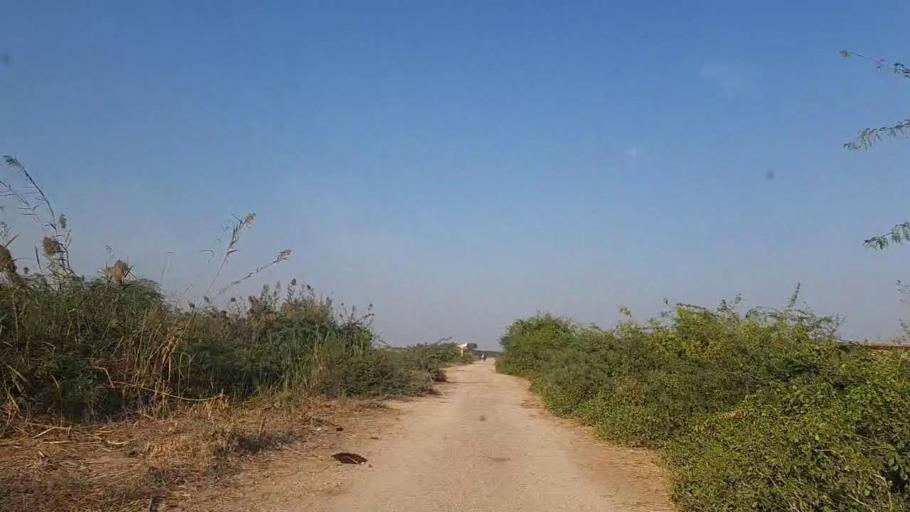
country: PK
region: Sindh
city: Thatta
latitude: 24.7221
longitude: 67.9461
